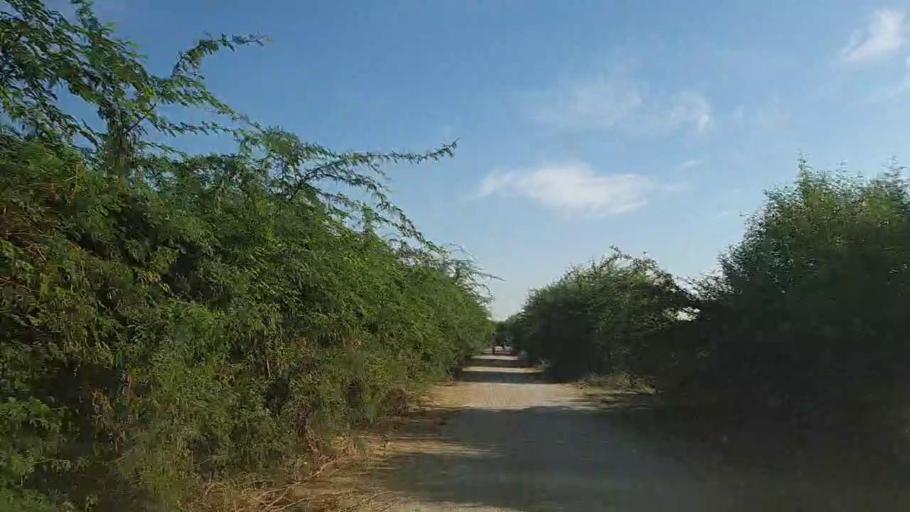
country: PK
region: Sindh
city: Bulri
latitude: 24.7868
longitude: 68.3490
